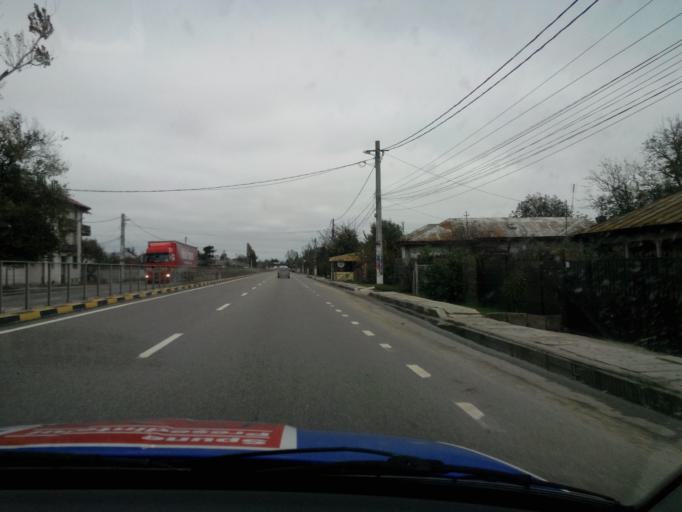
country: RO
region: Giurgiu
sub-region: Comuna Calugareni
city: Calugareni
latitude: 44.1750
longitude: 25.9973
